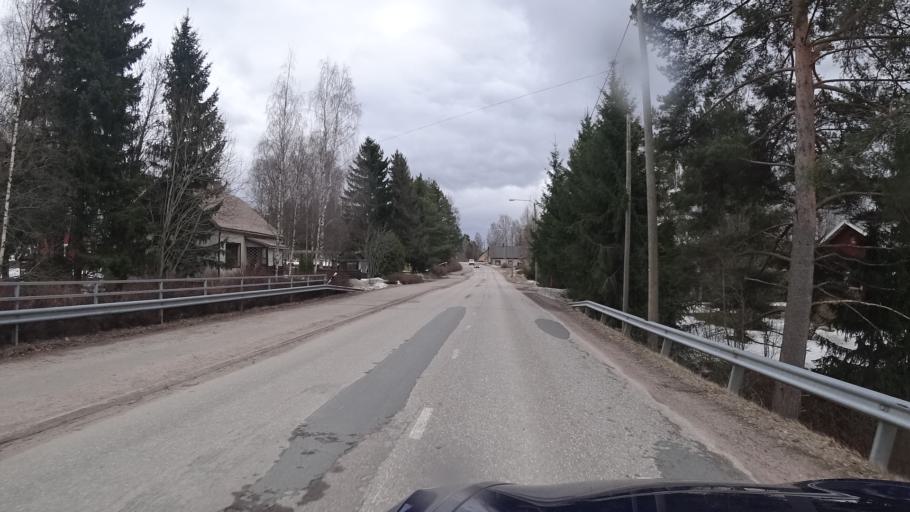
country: FI
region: Paijanne Tavastia
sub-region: Lahti
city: Nastola
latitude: 60.8757
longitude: 26.0011
